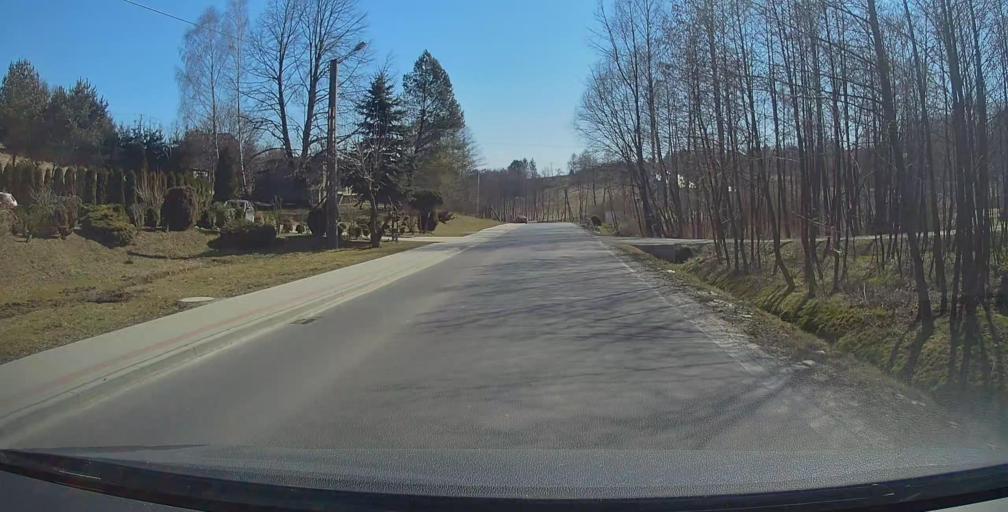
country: PL
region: Subcarpathian Voivodeship
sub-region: Powiat rzeszowski
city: Hyzne
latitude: 49.8887
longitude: 22.2277
